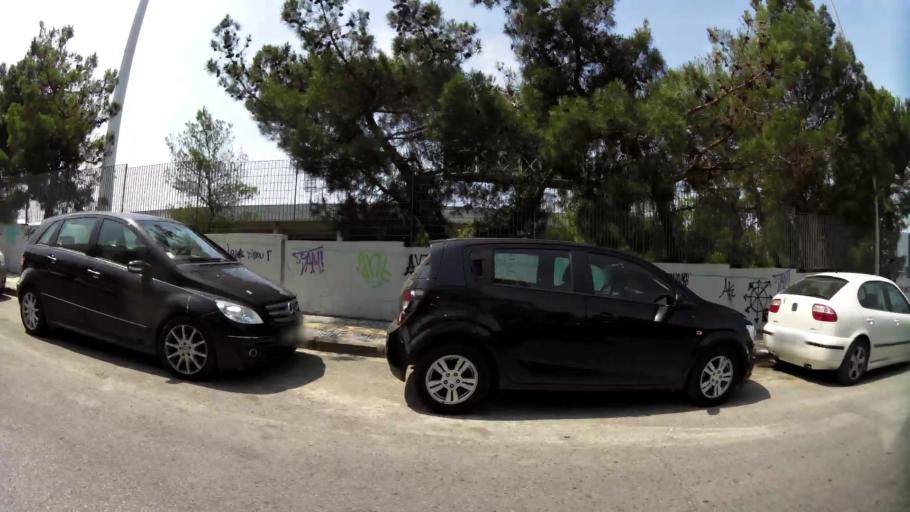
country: GR
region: Central Macedonia
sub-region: Nomos Thessalonikis
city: Triandria
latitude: 40.6269
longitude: 22.9671
